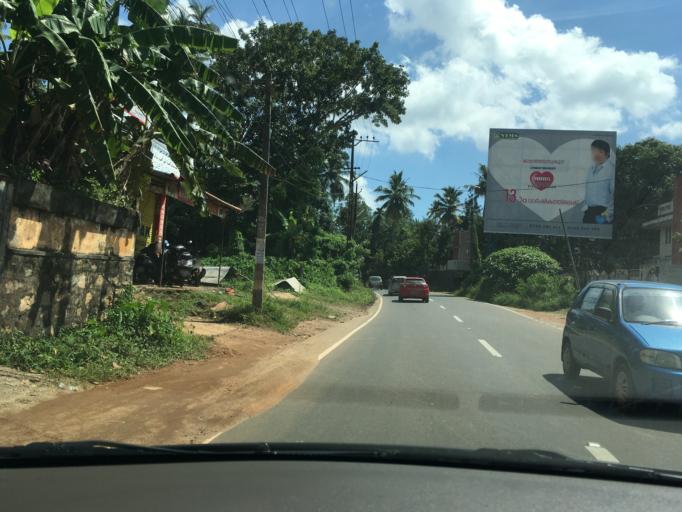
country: IN
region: Kerala
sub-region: Thiruvananthapuram
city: Nedumangad
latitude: 8.5982
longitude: 76.9956
